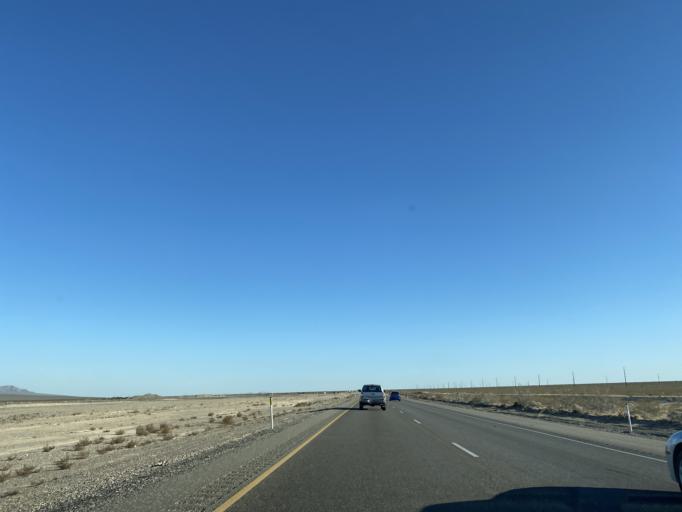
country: US
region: Nevada
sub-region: Clark County
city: Summerlin South
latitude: 36.4032
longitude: -115.4012
